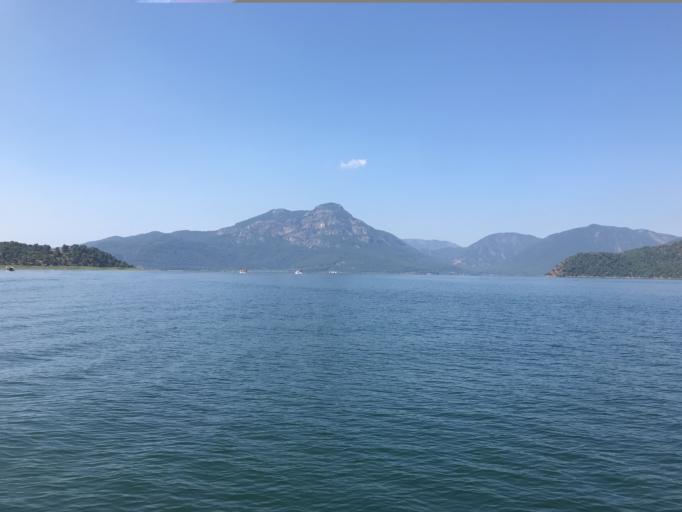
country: TR
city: Dalyan
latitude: 36.9068
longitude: 28.6500
